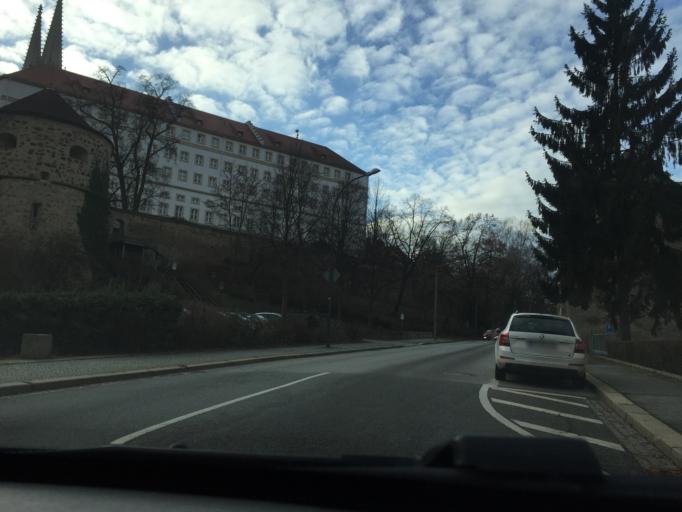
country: DE
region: Saxony
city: Goerlitz
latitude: 51.1600
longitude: 14.9922
